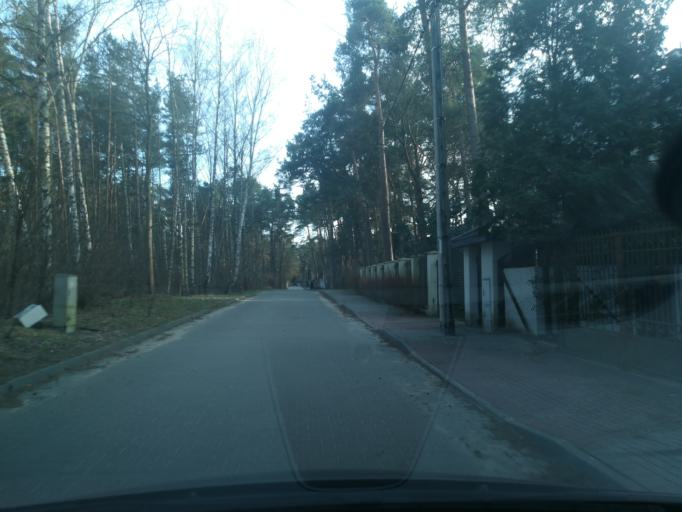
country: PL
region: Masovian Voivodeship
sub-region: Powiat piaseczynski
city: Konstancin-Jeziorna
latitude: 52.0801
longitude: 21.1069
